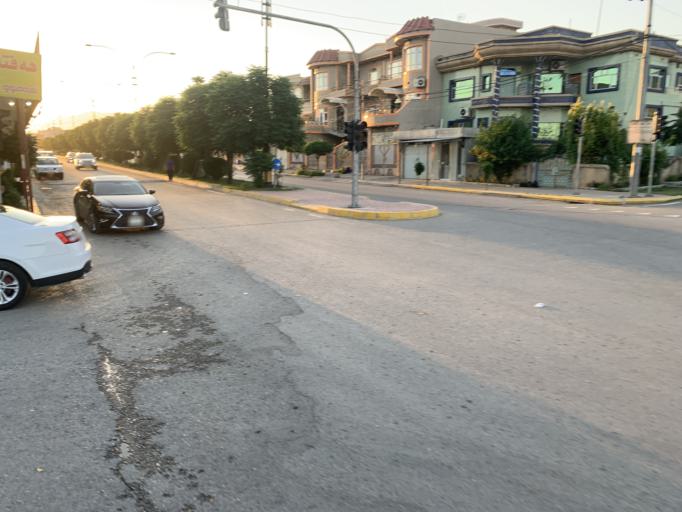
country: IQ
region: As Sulaymaniyah
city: Raniye
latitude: 36.2457
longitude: 44.8783
